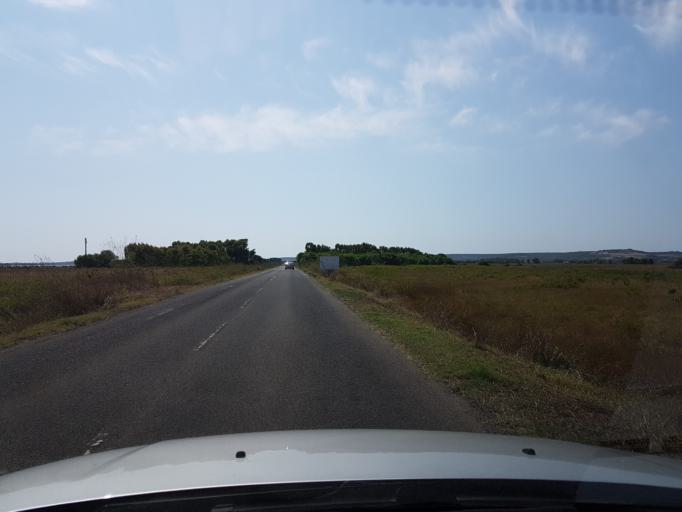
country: IT
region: Sardinia
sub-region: Provincia di Oristano
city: Cabras
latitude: 39.9170
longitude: 8.4873
